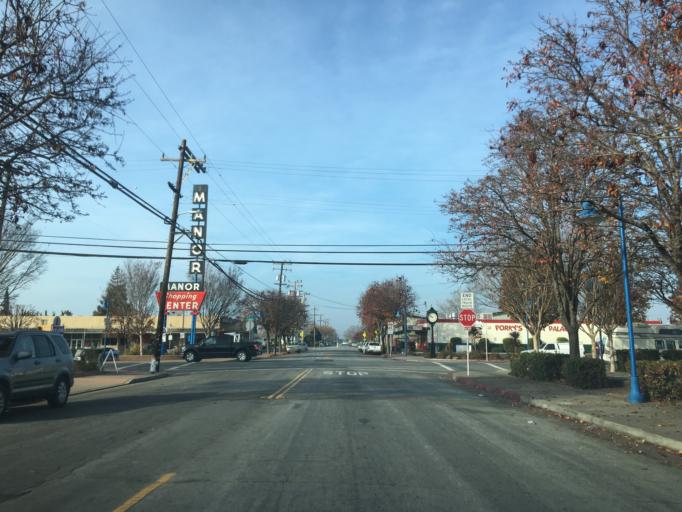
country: US
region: California
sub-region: Alameda County
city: San Lorenzo
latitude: 37.6913
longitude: -122.1513
